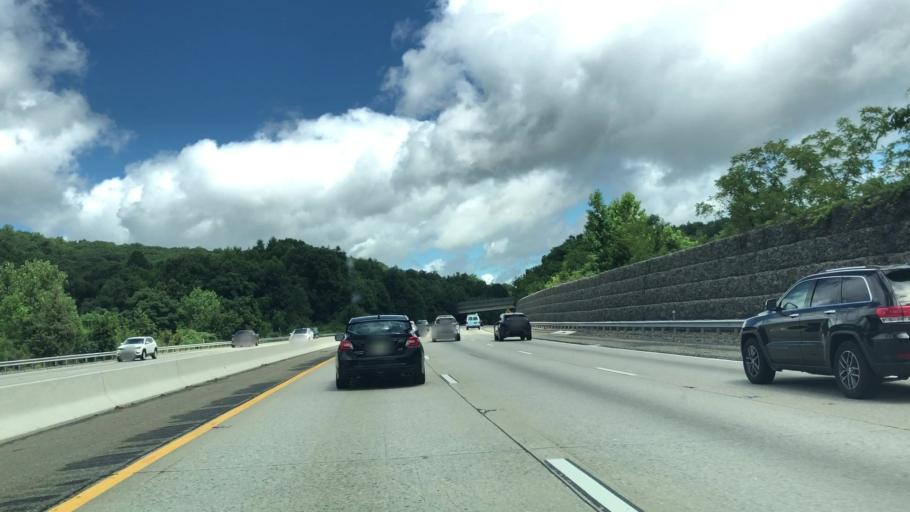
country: US
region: New Jersey
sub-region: Morris County
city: Lincoln Park
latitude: 40.9311
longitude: -74.3571
